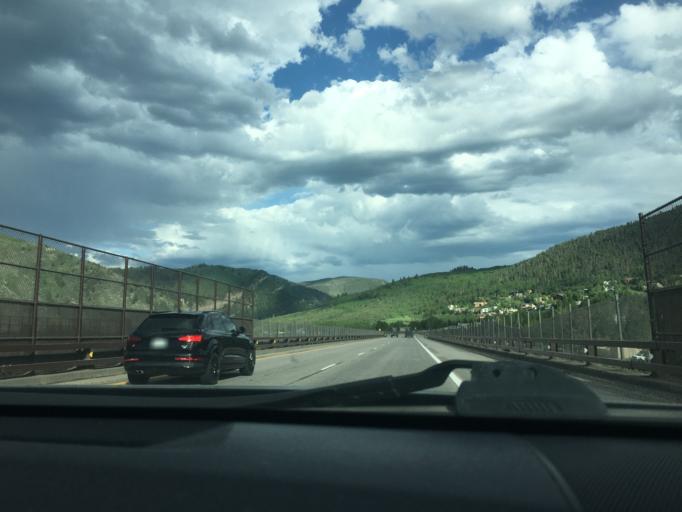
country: US
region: Colorado
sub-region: Eagle County
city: Avon
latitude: 39.6234
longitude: -106.4861
